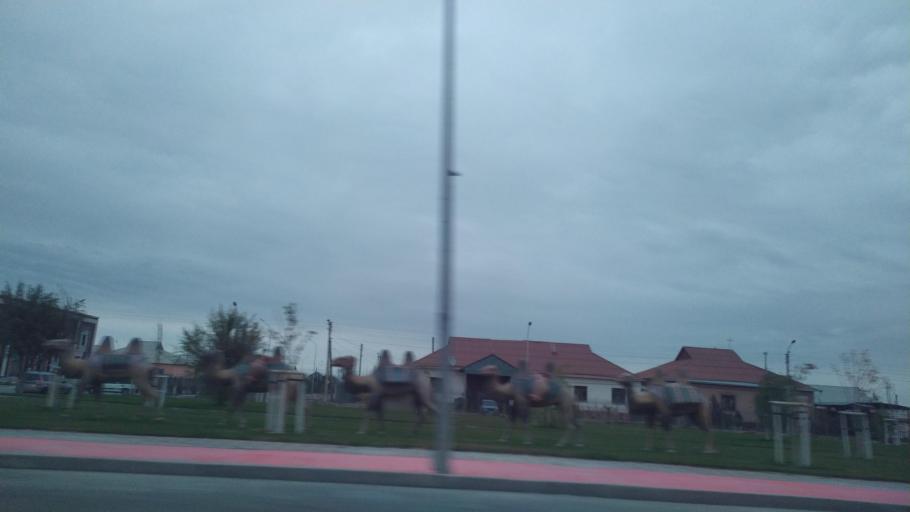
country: KZ
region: Ongtustik Qazaqstan
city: Turkestan
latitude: 43.2817
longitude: 68.3173
